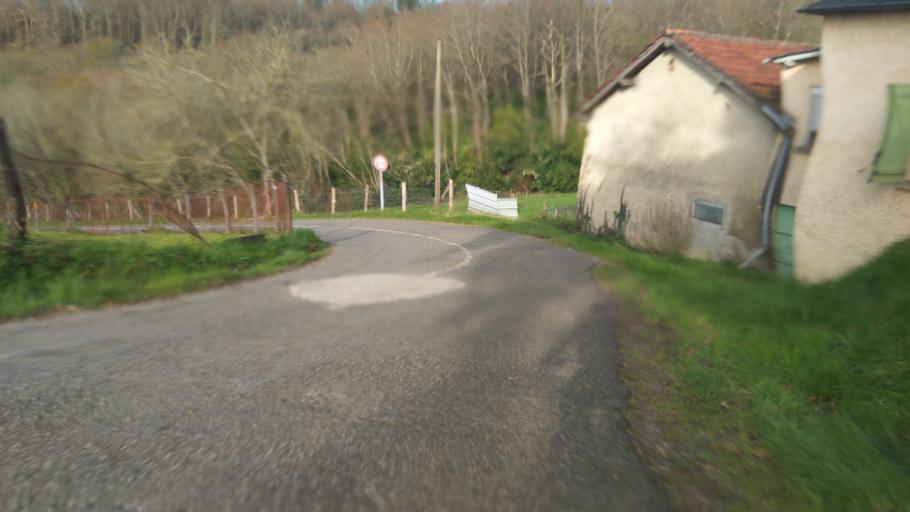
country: FR
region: Aquitaine
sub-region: Departement des Pyrenees-Atlantiques
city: Mazeres-Lezons
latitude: 43.2616
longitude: -0.3553
